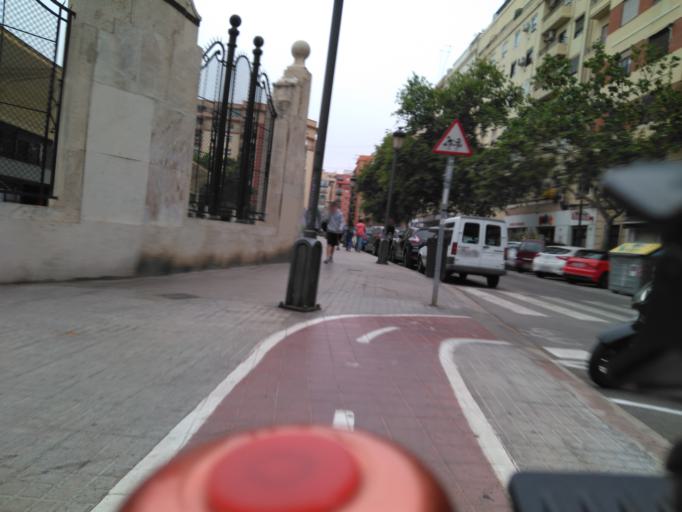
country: ES
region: Valencia
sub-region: Provincia de Valencia
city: Valencia
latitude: 39.4690
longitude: -0.3883
